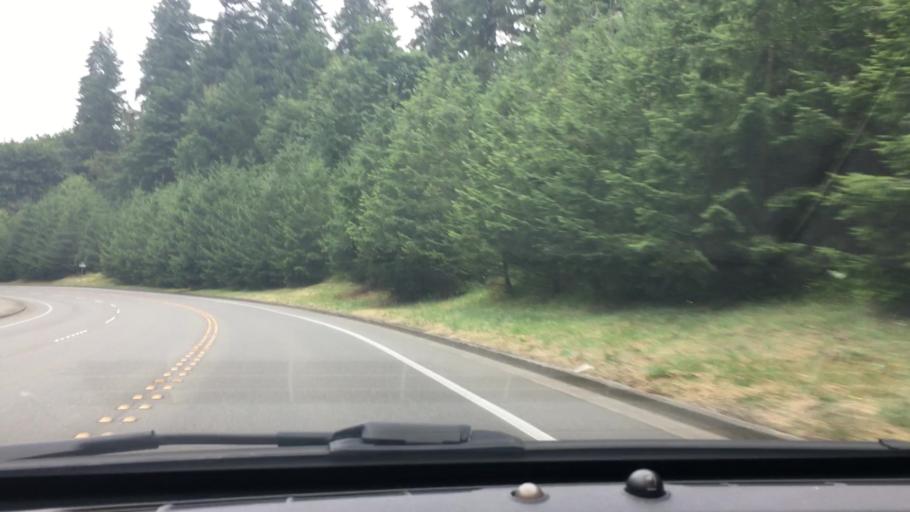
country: US
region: Washington
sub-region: King County
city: West Lake Sammamish
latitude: 47.5569
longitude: -122.1077
